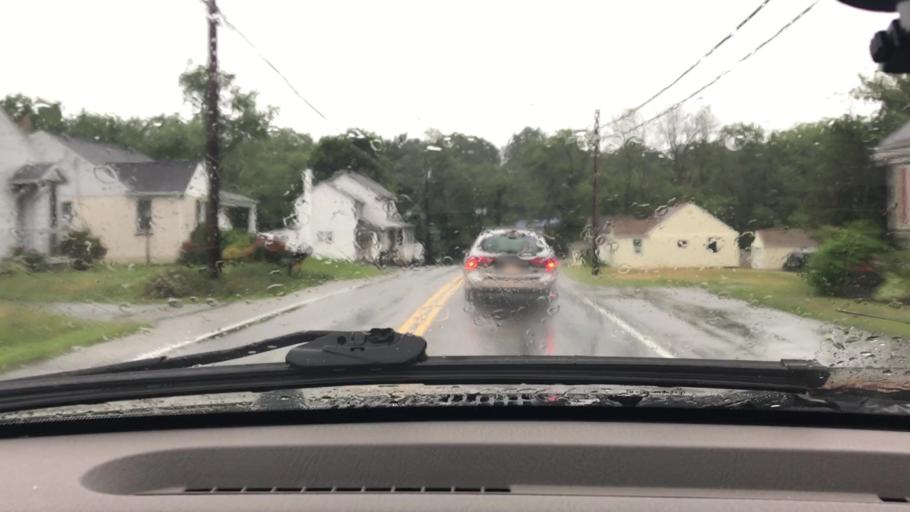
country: US
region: Pennsylvania
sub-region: Lancaster County
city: Elizabethtown
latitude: 40.1473
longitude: -76.6262
